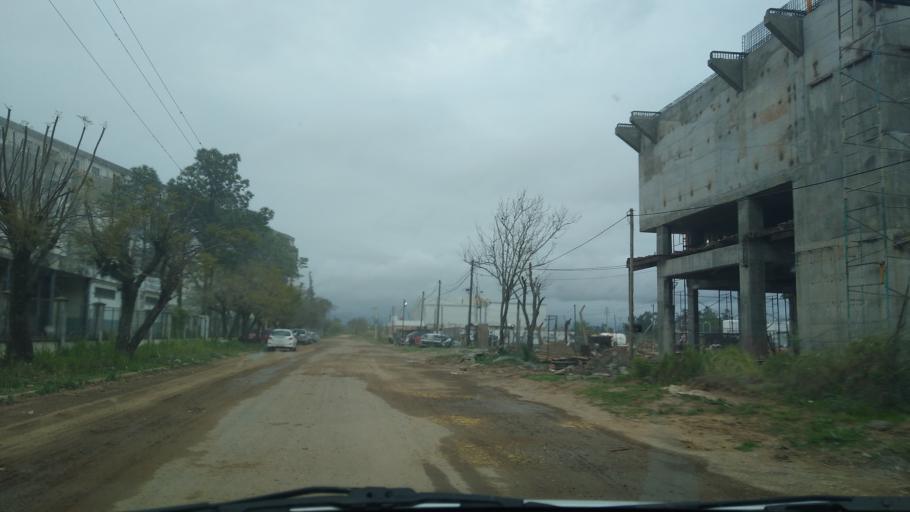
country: AR
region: Chaco
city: Barranqueras
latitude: -27.4721
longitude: -58.9100
